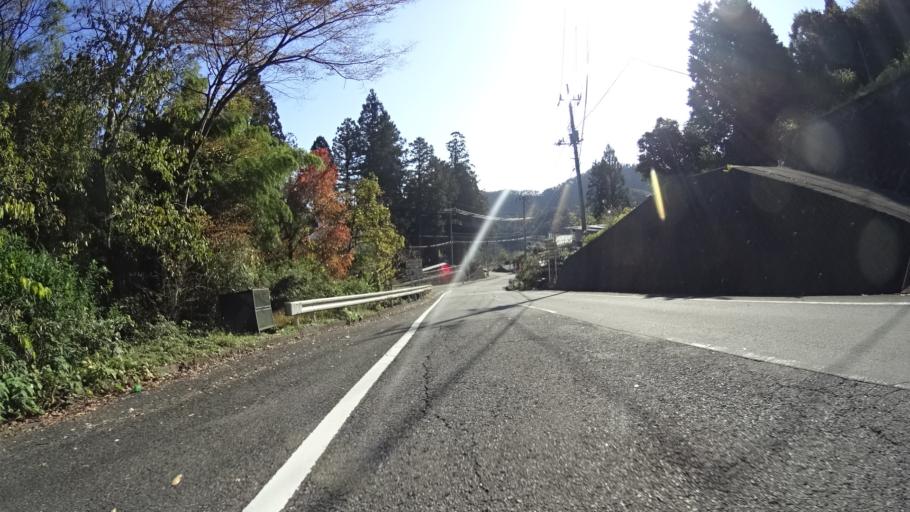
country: JP
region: Yamanashi
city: Uenohara
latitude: 35.6577
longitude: 139.1197
